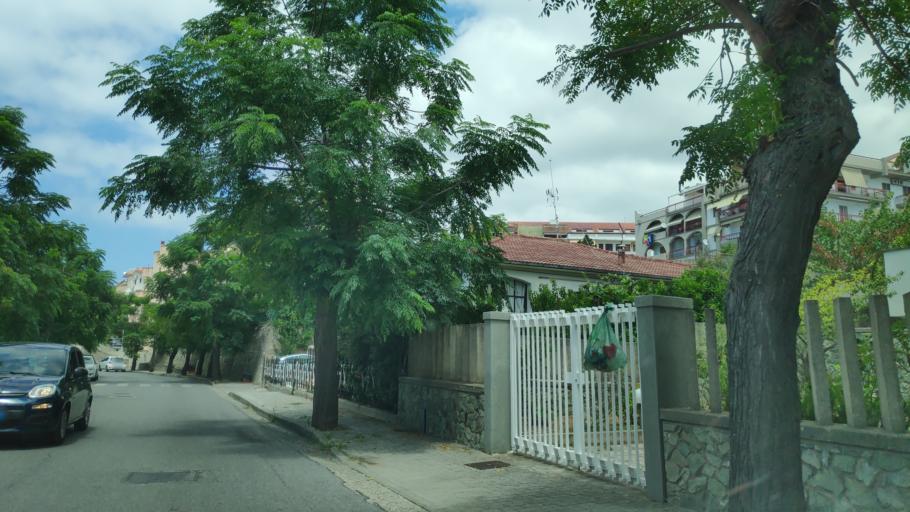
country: IT
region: Calabria
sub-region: Provincia di Cosenza
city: Paola
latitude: 39.3593
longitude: 16.0367
